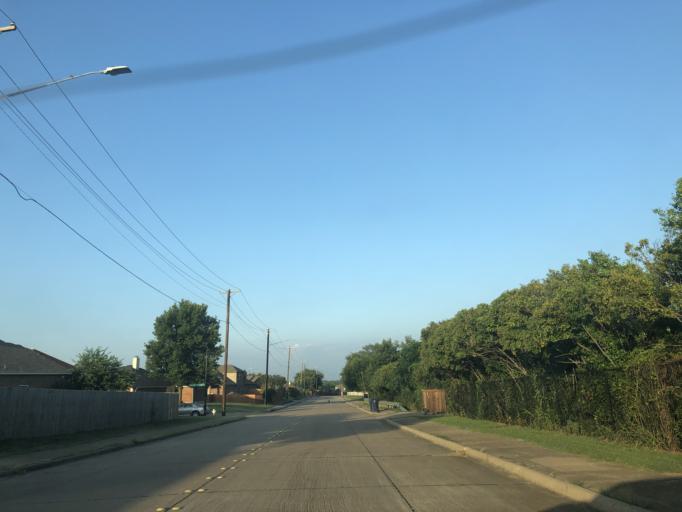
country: US
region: Texas
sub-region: Dallas County
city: Sunnyvale
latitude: 32.8387
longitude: -96.5637
